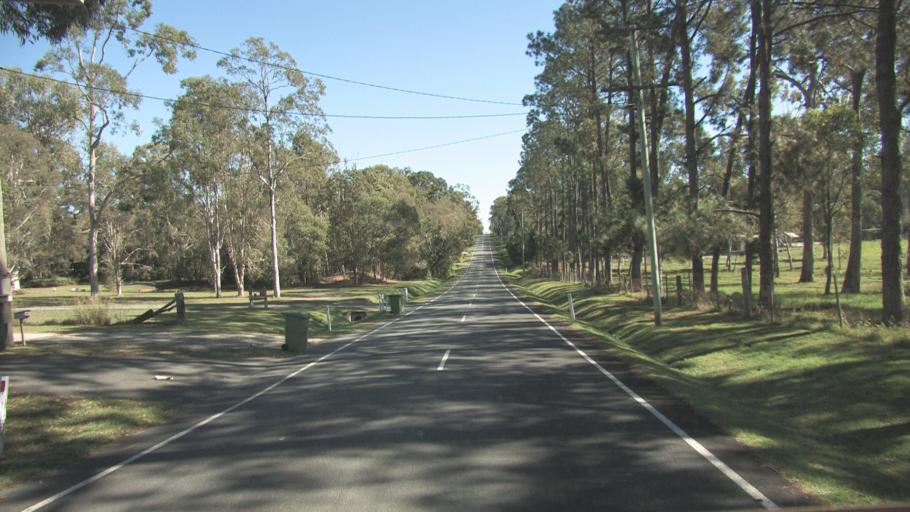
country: AU
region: Queensland
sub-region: Logan
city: Park Ridge South
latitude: -27.7075
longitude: 153.0489
